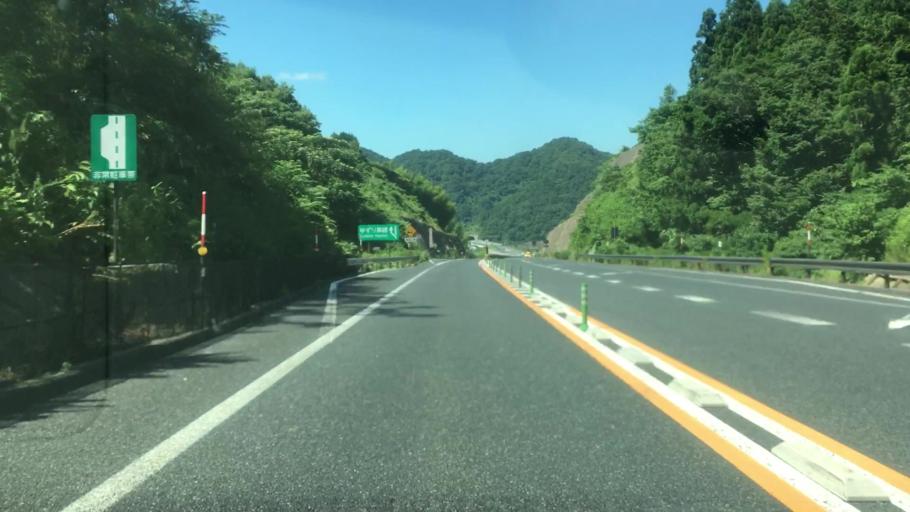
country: JP
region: Tottori
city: Tottori
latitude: 35.3693
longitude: 134.2028
